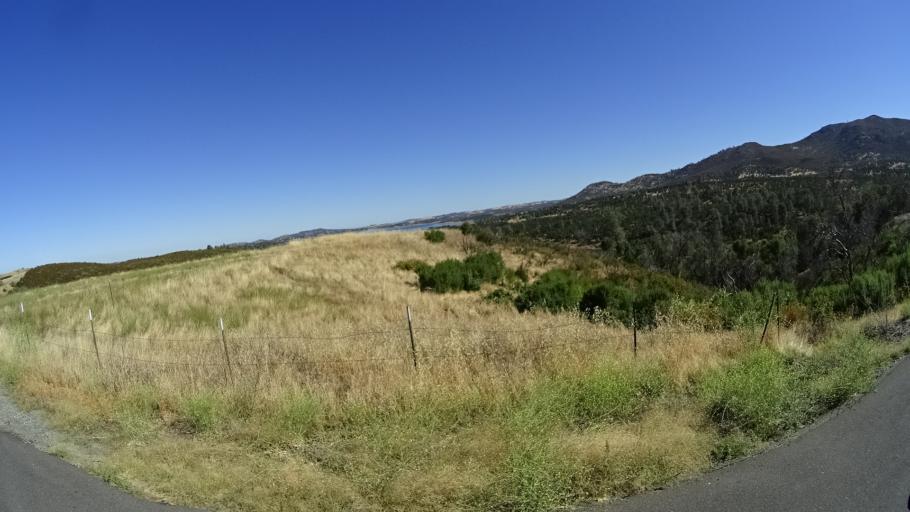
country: US
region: California
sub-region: Calaveras County
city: Rancho Calaveras
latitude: 38.1141
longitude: -120.7854
